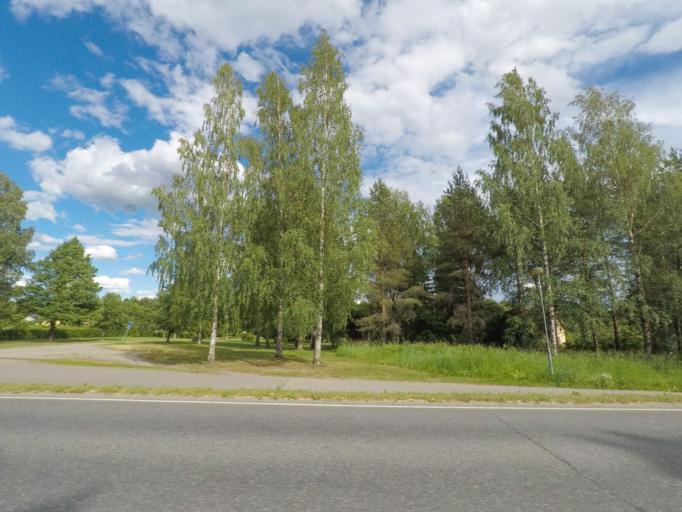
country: FI
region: Paijanne Tavastia
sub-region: Lahti
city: Lahti
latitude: 60.9636
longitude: 25.6240
